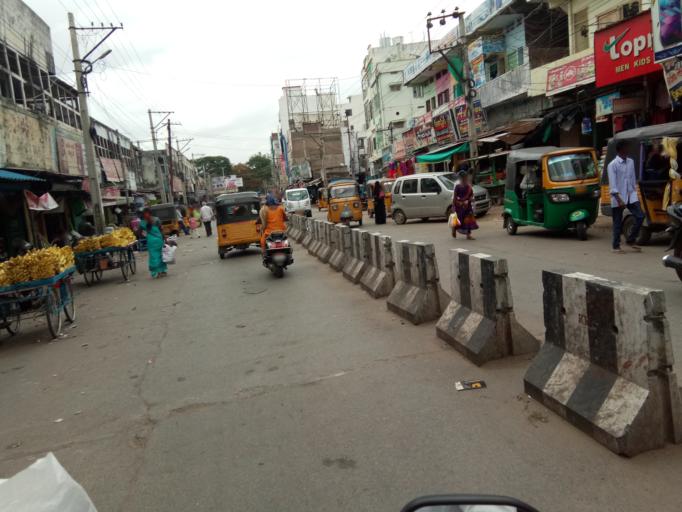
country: IN
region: Telangana
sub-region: Khammam
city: Khammam
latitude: 17.2498
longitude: 80.1426
